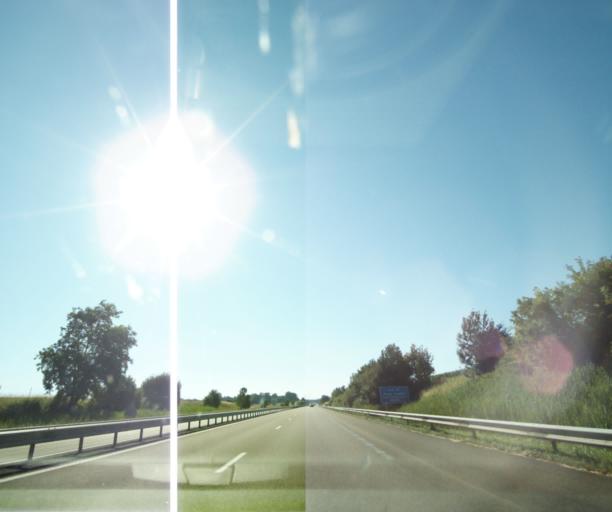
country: FR
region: Champagne-Ardenne
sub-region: Departement de l'Aube
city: Verrieres
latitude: 48.2228
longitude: 4.2101
